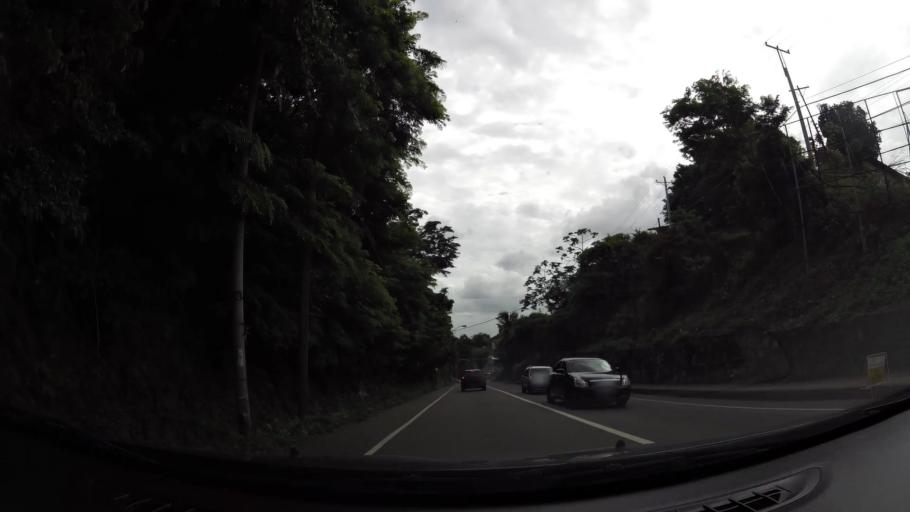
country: TT
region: San Juan/Laventille
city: Laventille
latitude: 10.6692
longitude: -61.4896
